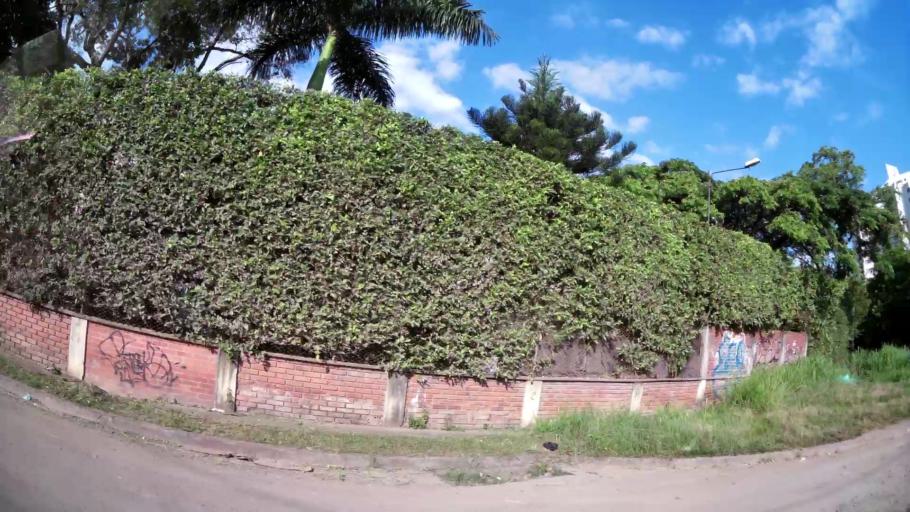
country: CO
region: Valle del Cauca
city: Cali
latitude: 3.4190
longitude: -76.5417
